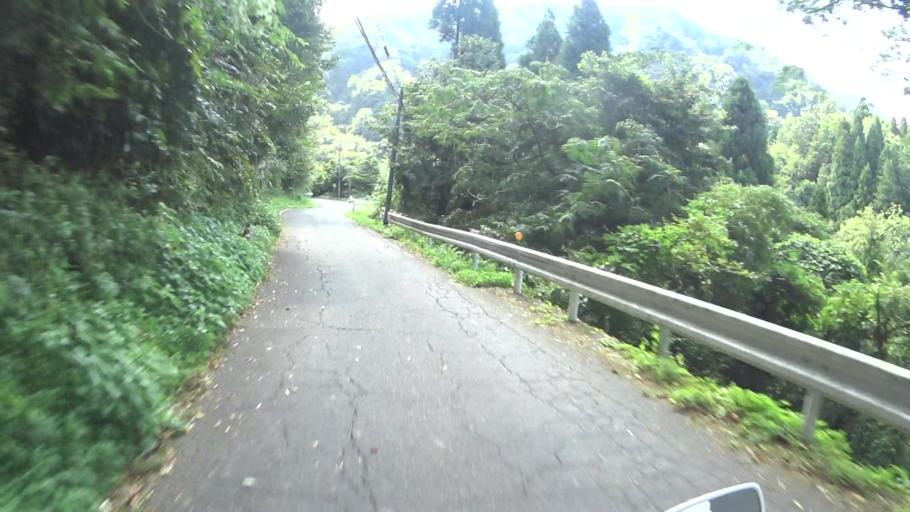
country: JP
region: Kyoto
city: Miyazu
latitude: 35.6355
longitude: 135.1951
